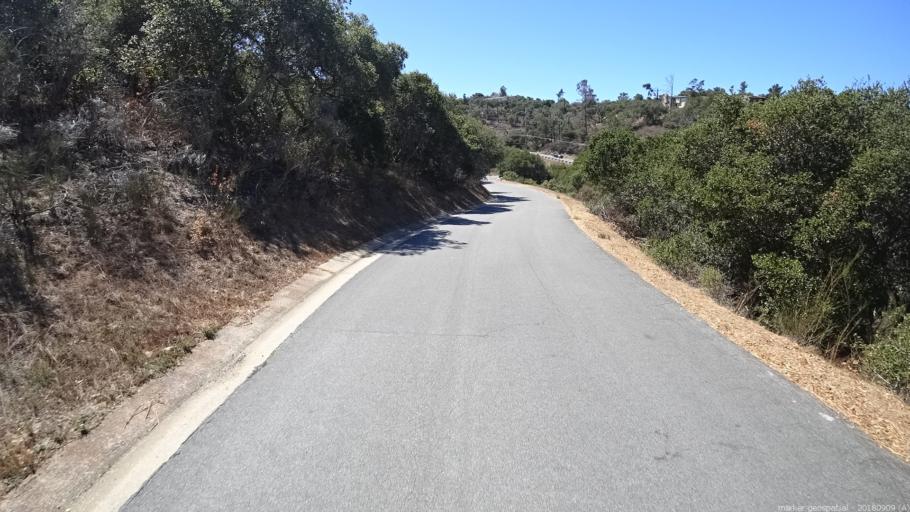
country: US
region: California
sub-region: Monterey County
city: Carmel Valley Village
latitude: 36.5617
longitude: -121.7485
